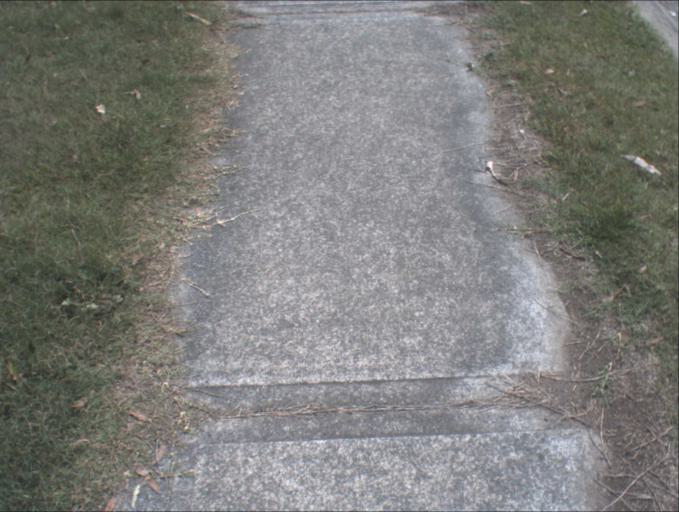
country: AU
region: Queensland
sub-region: Logan
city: Beenleigh
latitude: -27.7179
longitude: 153.1892
